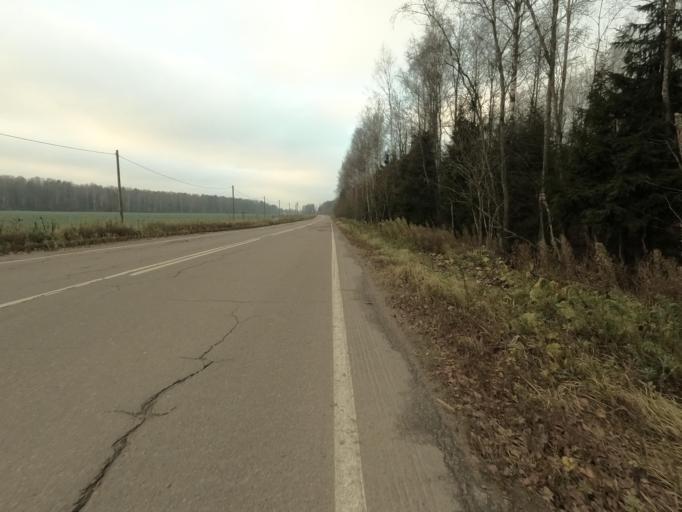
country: RU
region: Leningrad
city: Mga
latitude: 59.7974
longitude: 31.0022
